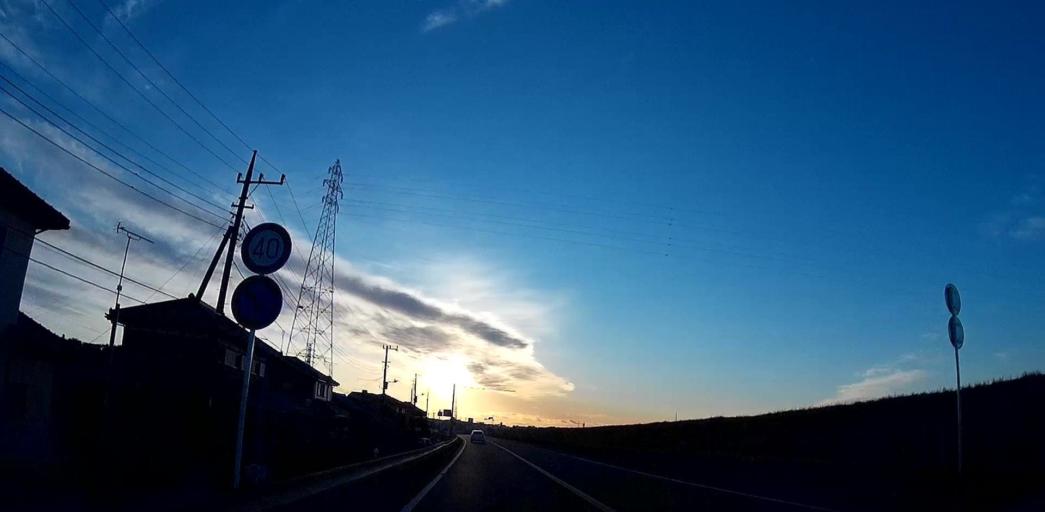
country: JP
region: Chiba
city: Katori-shi
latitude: 35.8993
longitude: 140.5209
